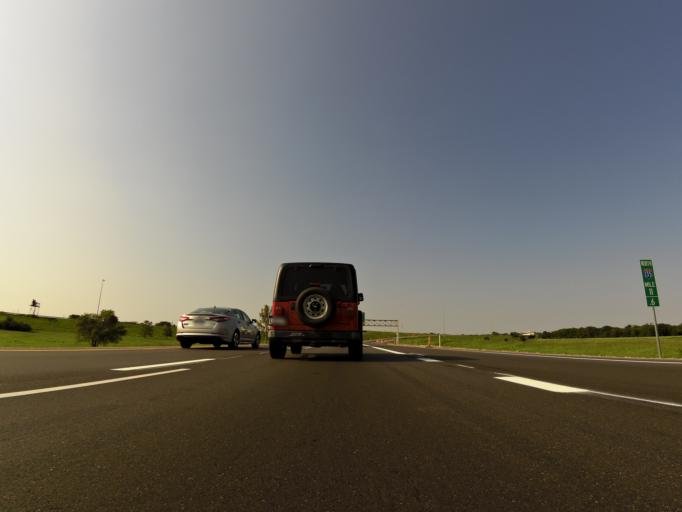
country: US
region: Kansas
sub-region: Sedgwick County
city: Park City
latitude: 37.7585
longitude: -97.3202
